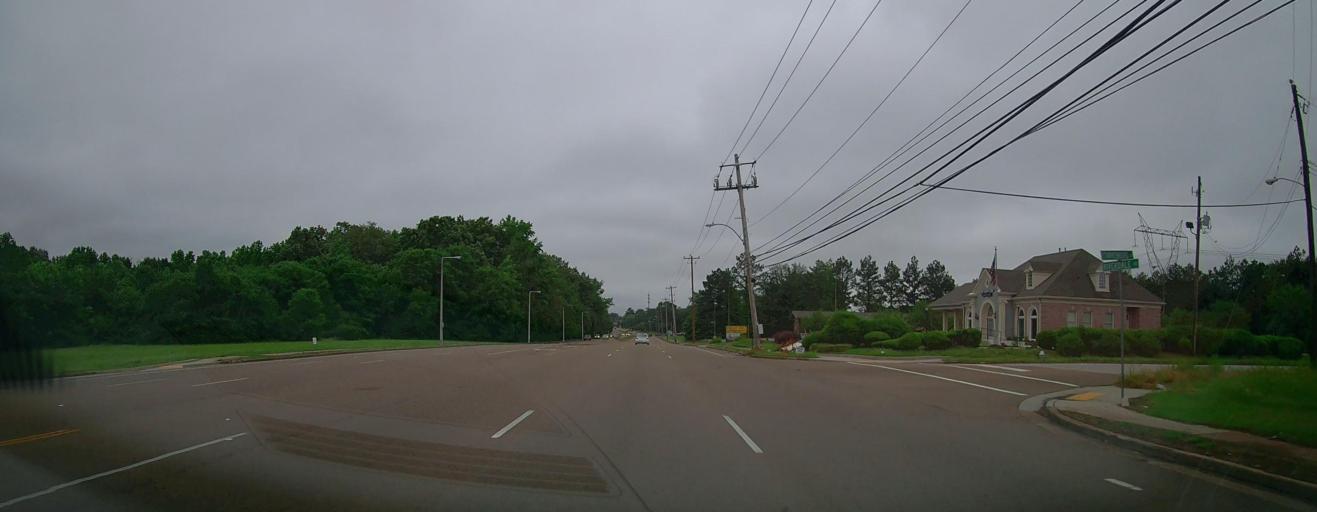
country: US
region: Tennessee
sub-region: Shelby County
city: Germantown
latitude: 35.0460
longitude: -89.8306
